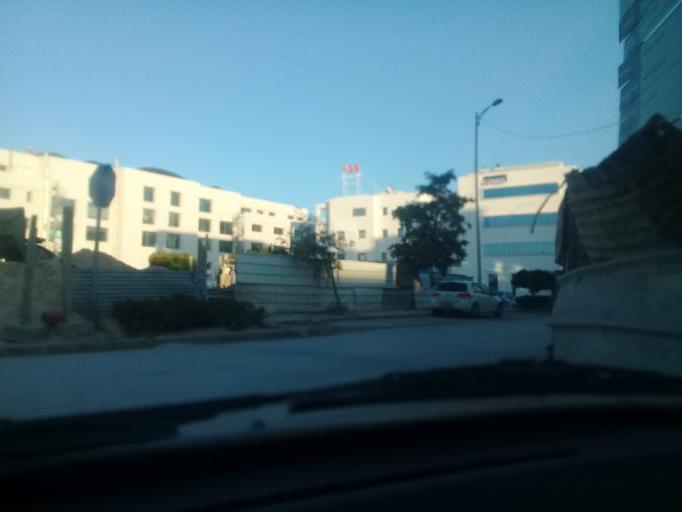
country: TN
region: Tunis
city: La Goulette
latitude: 36.8463
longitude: 10.2710
